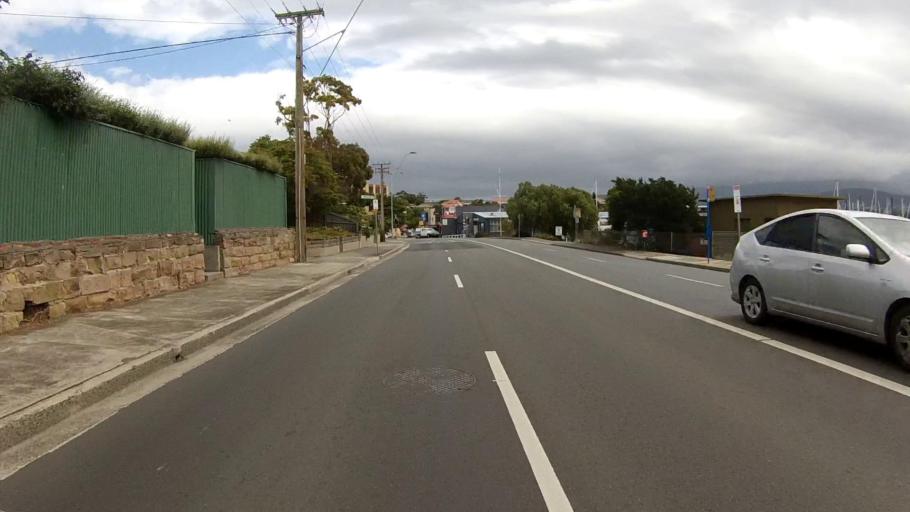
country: AU
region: Tasmania
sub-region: Clarence
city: Bellerive
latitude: -42.8734
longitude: 147.3691
